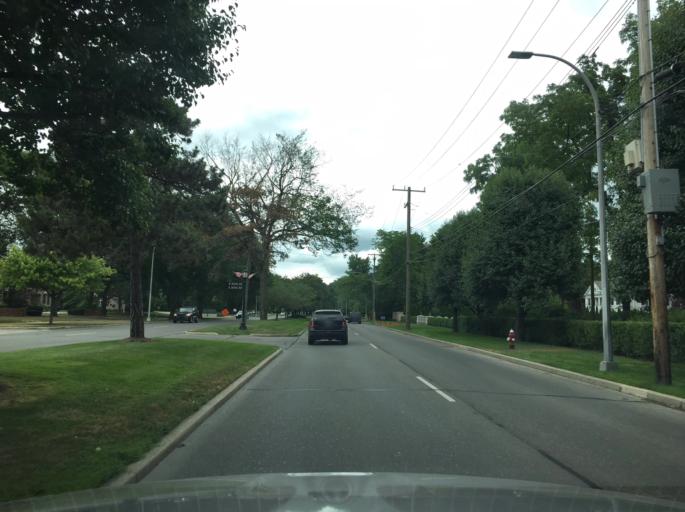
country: US
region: Michigan
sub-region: Wayne County
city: Grosse Pointe Shores
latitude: 42.4489
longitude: -82.8739
